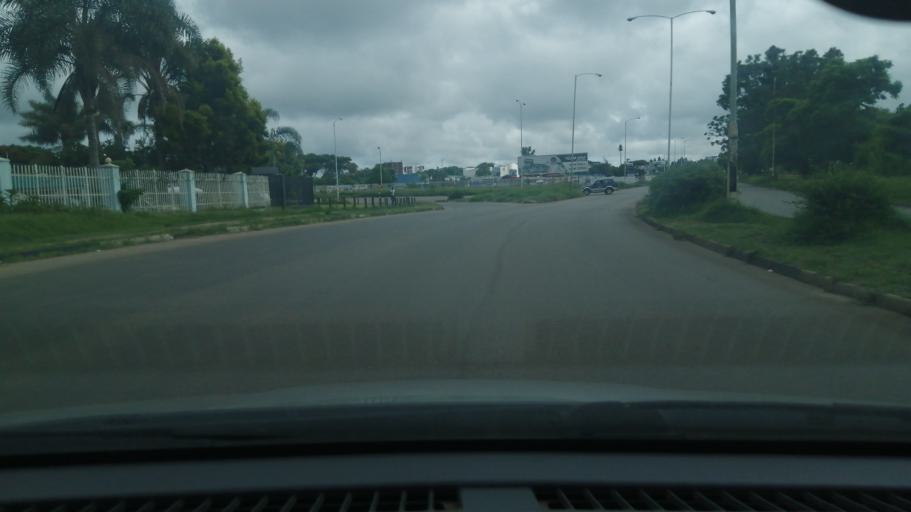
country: ZW
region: Harare
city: Harare
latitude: -17.8273
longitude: 31.0609
